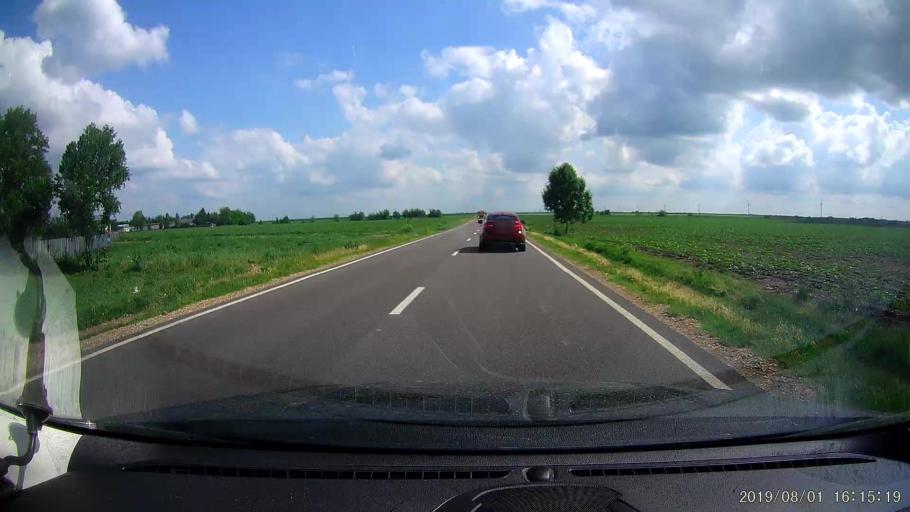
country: RO
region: Calarasi
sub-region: Comuna Stefan Voda
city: Stefan Voda
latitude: 44.3398
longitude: 27.3614
